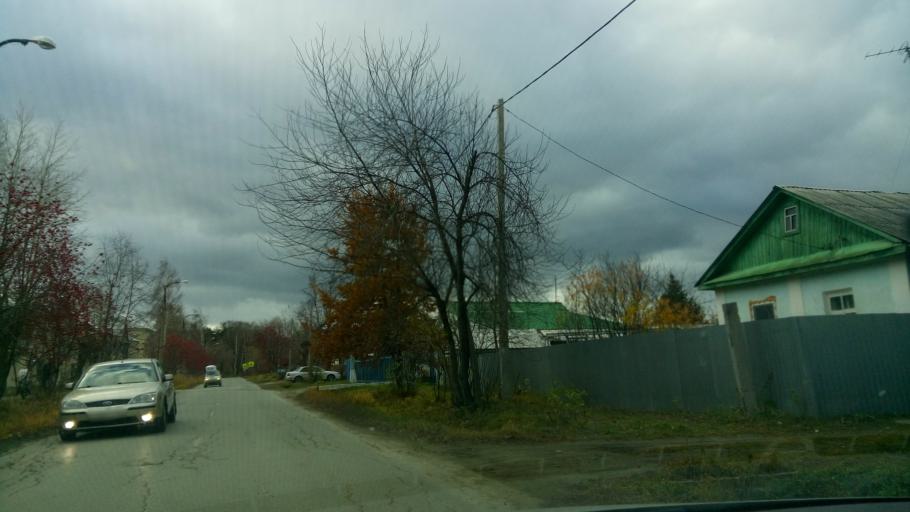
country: RU
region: Sverdlovsk
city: Sredneuralsk
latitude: 56.9917
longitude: 60.4732
